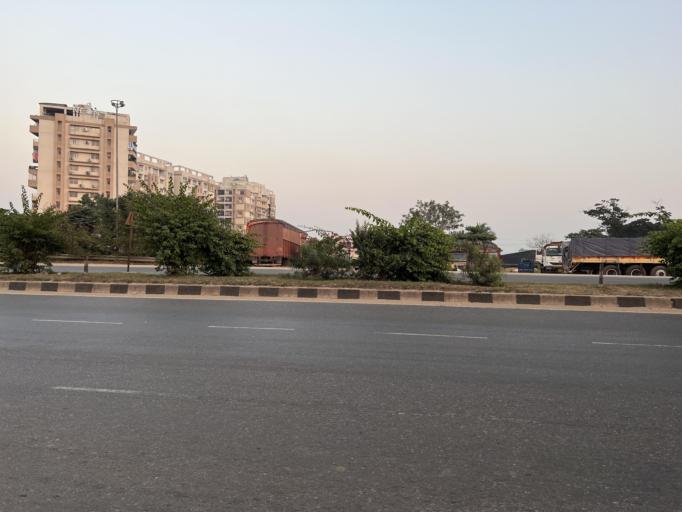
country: IN
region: Odisha
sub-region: Khordha
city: Bhubaneshwar
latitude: 20.3203
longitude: 85.8818
